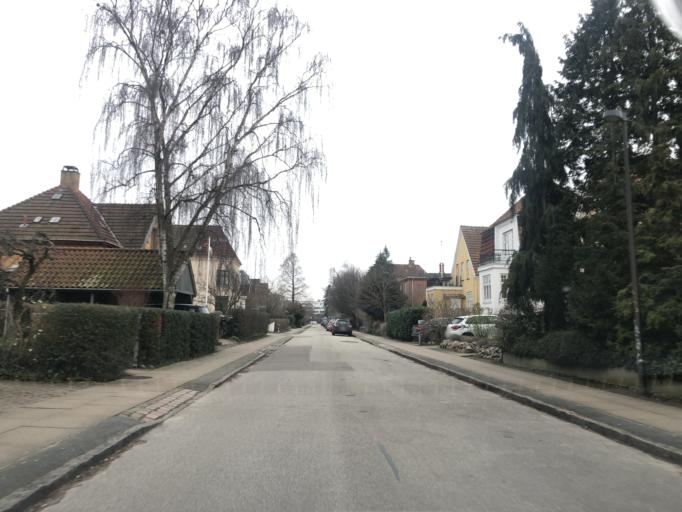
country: DK
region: Capital Region
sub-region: Frederiksberg Kommune
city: Frederiksberg
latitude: 55.6552
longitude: 12.5214
